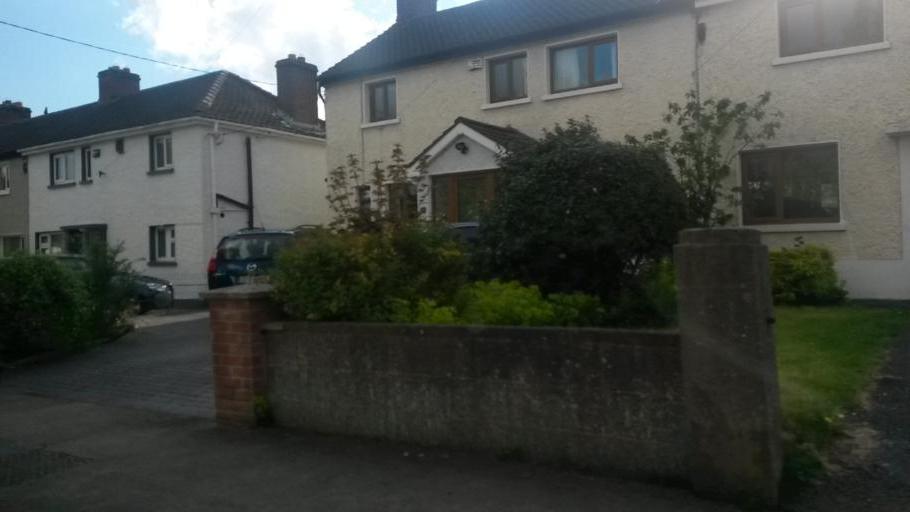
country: IE
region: Leinster
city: Glasnevin
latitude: 53.3851
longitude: -6.2671
